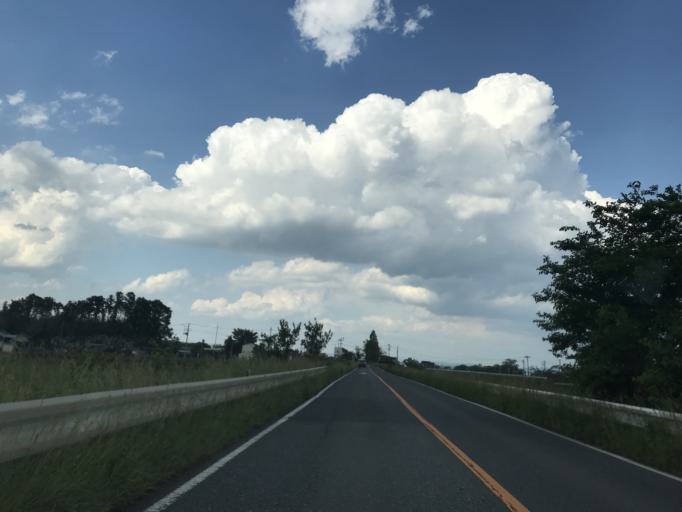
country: JP
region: Miyagi
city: Wakuya
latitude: 38.5946
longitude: 141.1661
